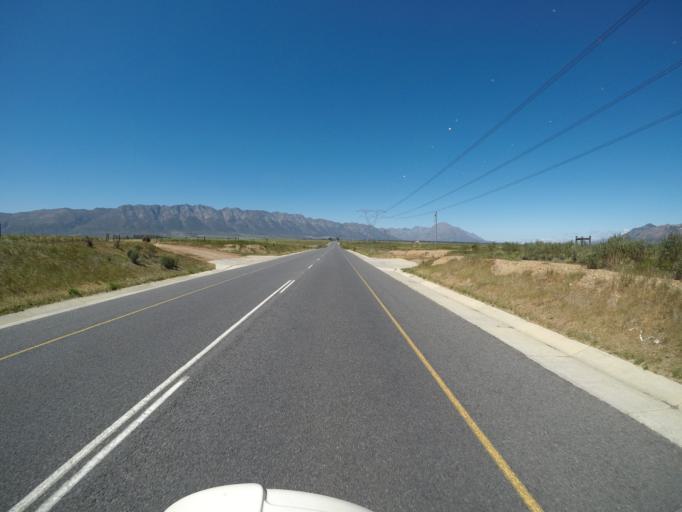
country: ZA
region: Western Cape
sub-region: Cape Winelands District Municipality
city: Ceres
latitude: -33.3120
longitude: 19.1209
